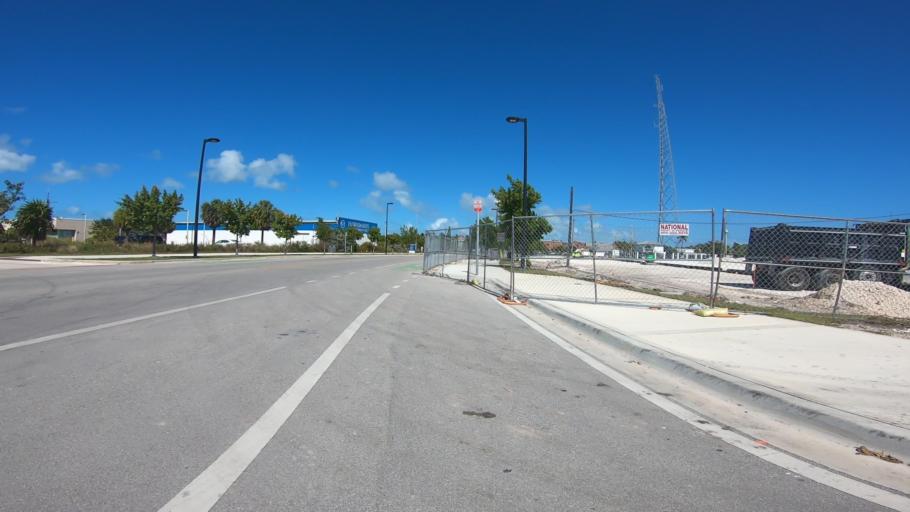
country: US
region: Florida
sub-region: Monroe County
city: Key West
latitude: 24.5497
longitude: -81.8073
